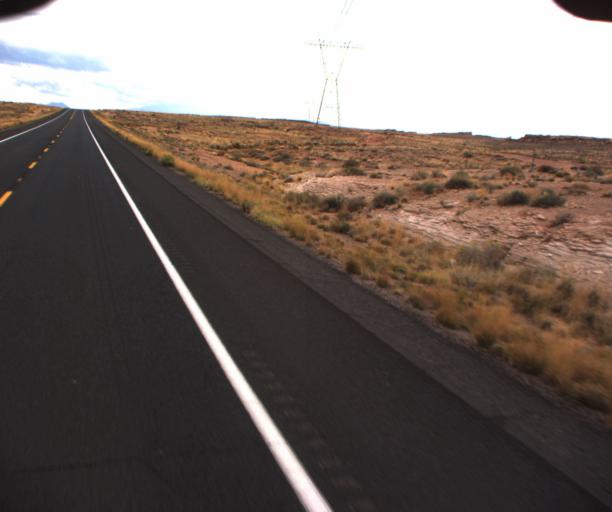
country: US
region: Arizona
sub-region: Coconino County
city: Tuba City
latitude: 35.8178
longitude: -111.4416
